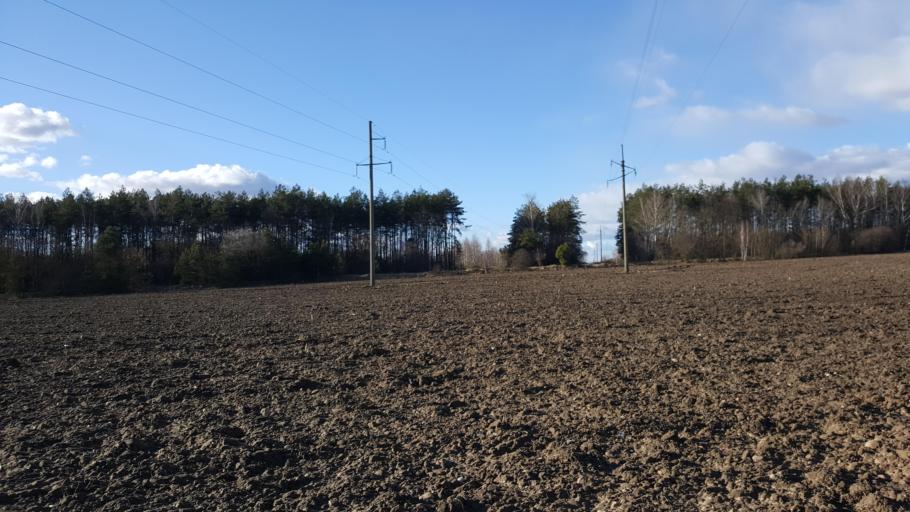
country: BY
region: Brest
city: Kamyanyets
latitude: 52.3838
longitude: 23.8462
